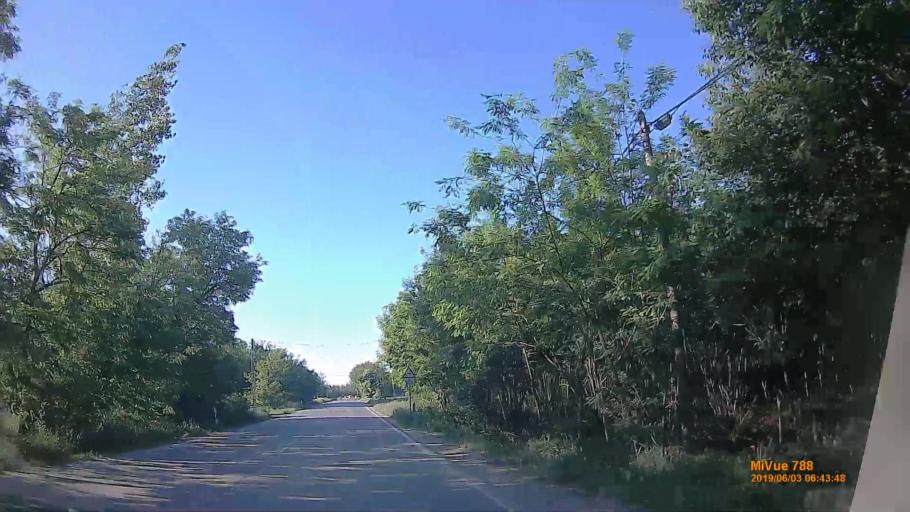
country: HU
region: Pest
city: Bugyi
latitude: 47.2510
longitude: 19.1272
